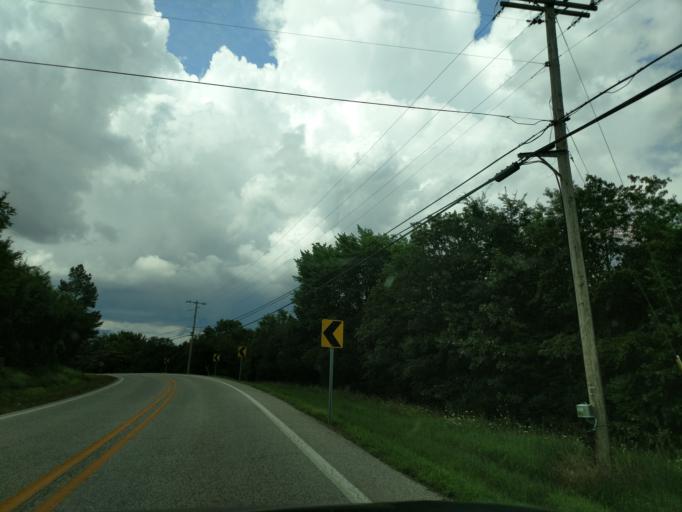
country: US
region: Arkansas
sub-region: Boone County
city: Harrison
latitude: 36.2448
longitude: -93.2111
